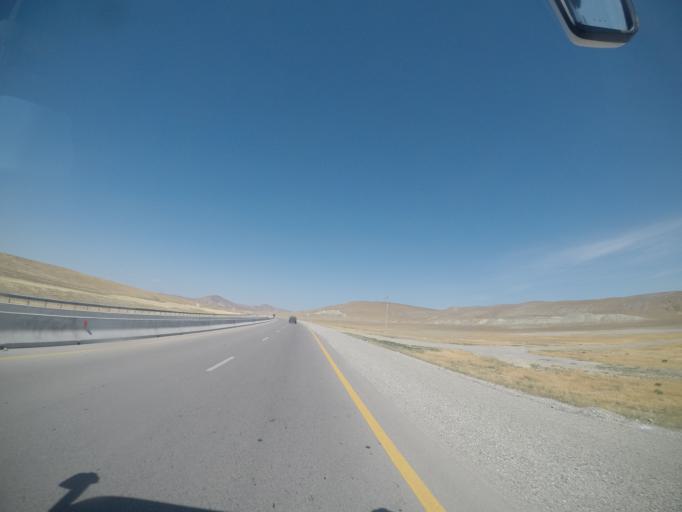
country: AZ
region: Sumqayit
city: Haci Zeynalabdin
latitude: 40.4947
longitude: 49.3602
